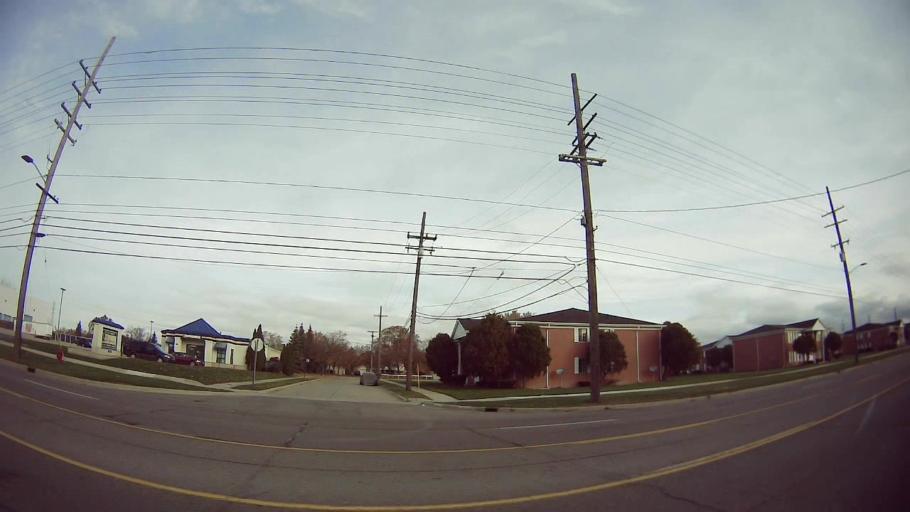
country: US
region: Michigan
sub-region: Macomb County
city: Warren
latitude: 42.4771
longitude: -83.0364
